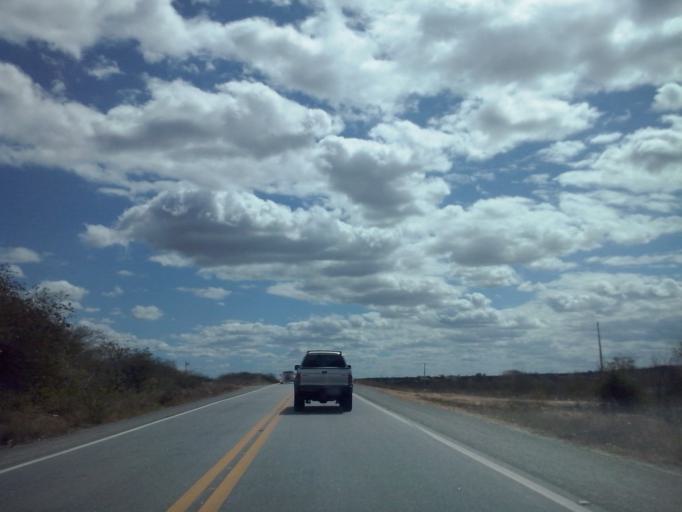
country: BR
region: Paraiba
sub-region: Soledade
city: Soledade
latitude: -7.0399
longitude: -36.4113
